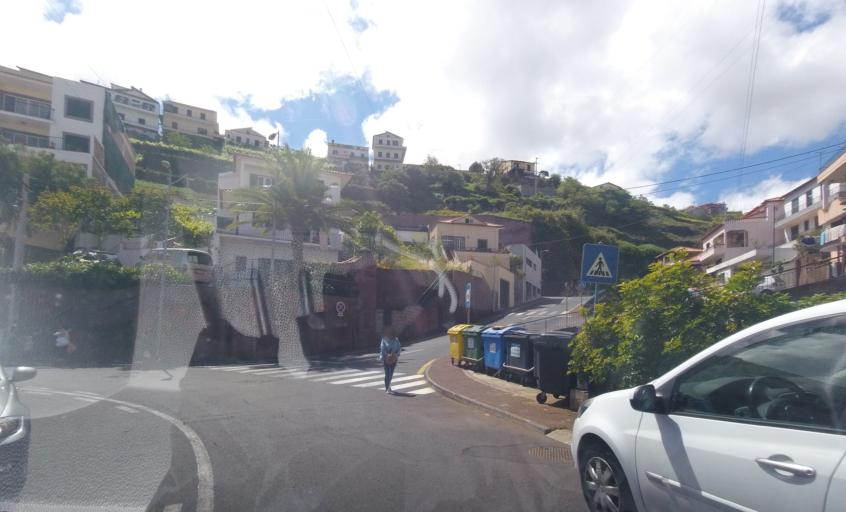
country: PT
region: Madeira
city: Camara de Lobos
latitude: 32.6744
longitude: -16.9783
